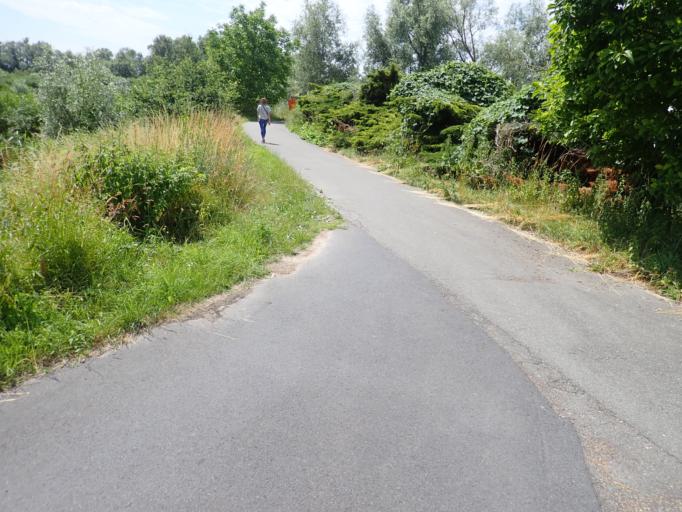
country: BE
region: Flanders
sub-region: Provincie Oost-Vlaanderen
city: Hamme
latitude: 51.1119
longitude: 4.1662
